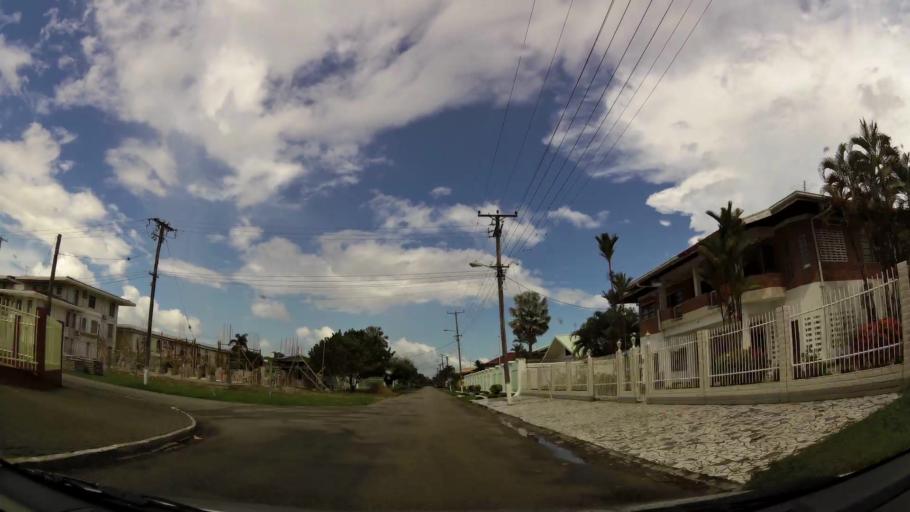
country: SR
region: Paramaribo
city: Paramaribo
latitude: 5.8356
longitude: -55.1298
